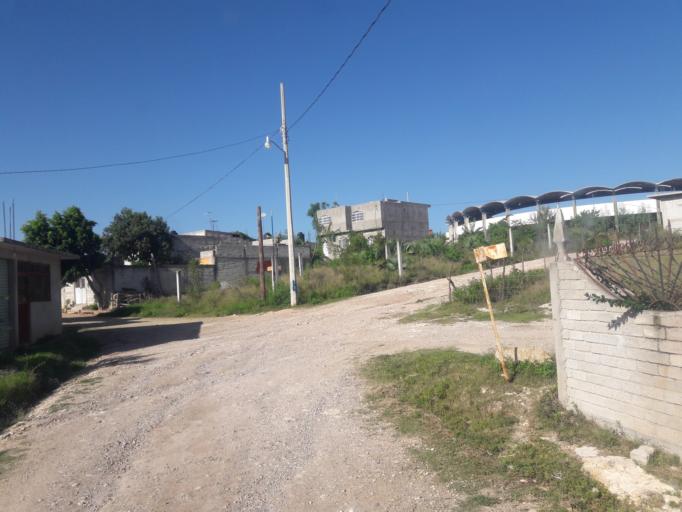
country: MX
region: Oaxaca
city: Ciudad de Huajuapam de Leon
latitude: 17.8050
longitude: -97.8065
